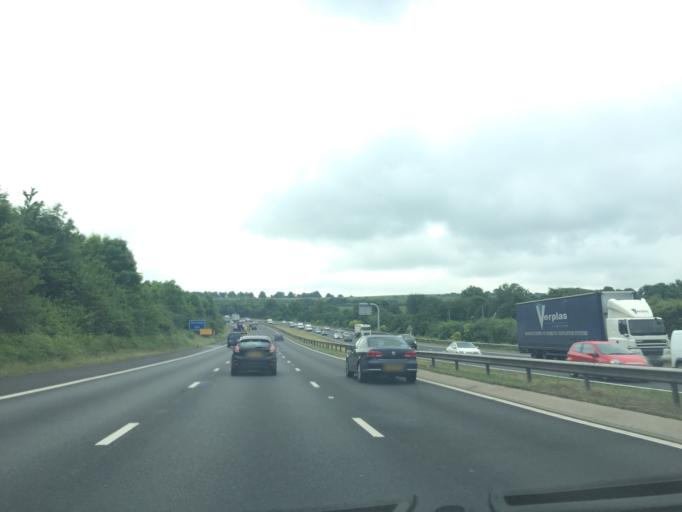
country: GB
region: England
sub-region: Hampshire
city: Winchester
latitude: 51.0526
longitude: -1.2986
